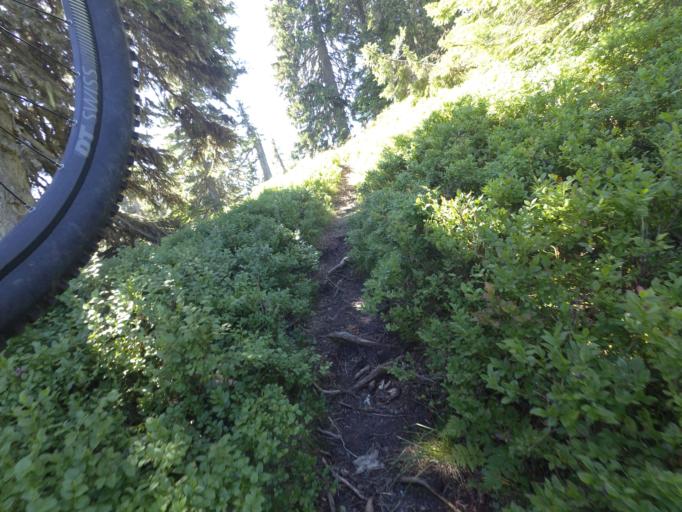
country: AT
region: Salzburg
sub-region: Politischer Bezirk Sankt Johann im Pongau
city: Goldegg
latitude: 47.3527
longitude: 13.0740
